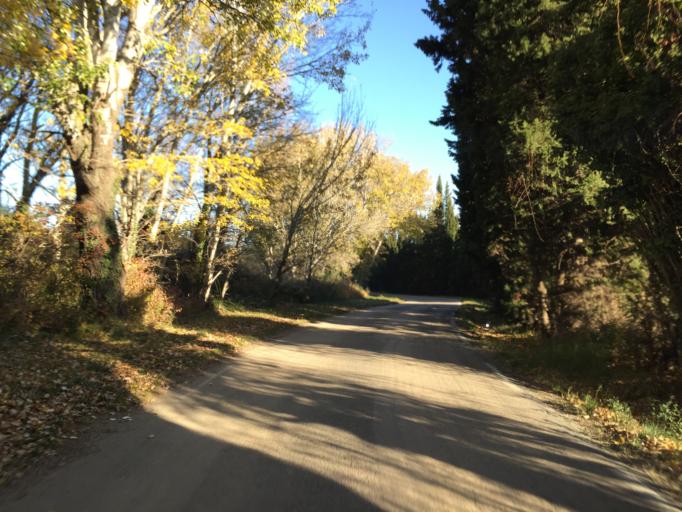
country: FR
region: Provence-Alpes-Cote d'Azur
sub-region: Departement du Vaucluse
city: Bedarrides
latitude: 44.0618
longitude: 4.9314
